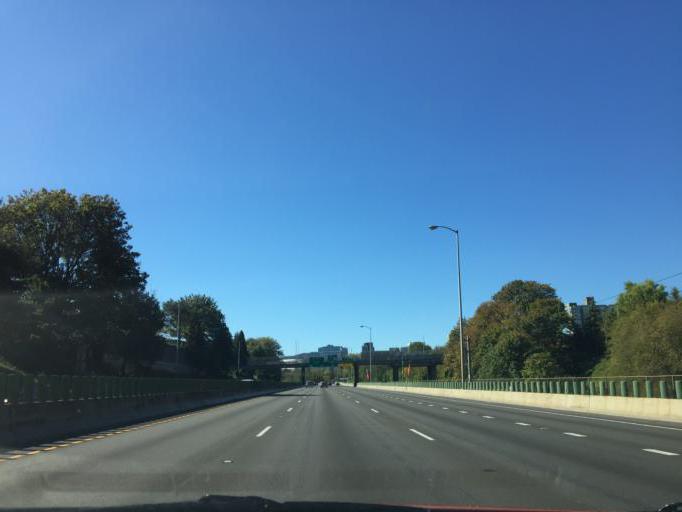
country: US
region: Oregon
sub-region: Multnomah County
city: Portland
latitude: 45.5302
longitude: -122.6418
